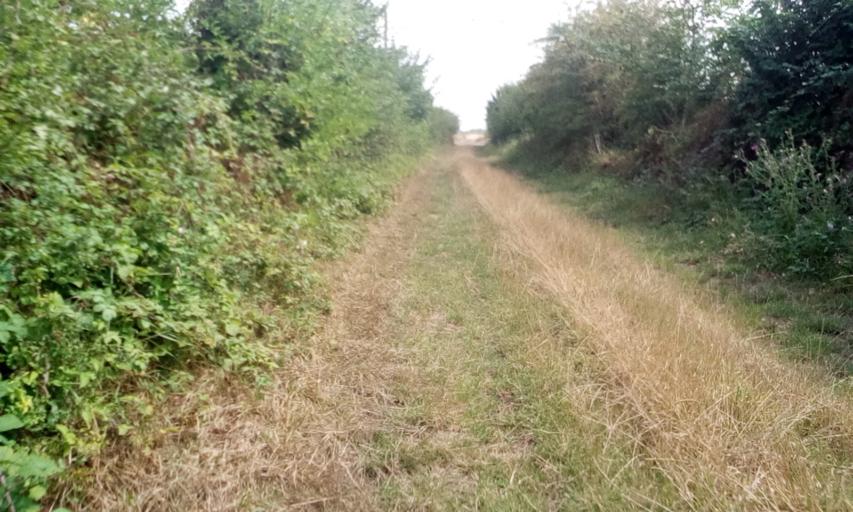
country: FR
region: Lower Normandy
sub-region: Departement du Calvados
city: Bellengreville
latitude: 49.1330
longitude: -0.2204
